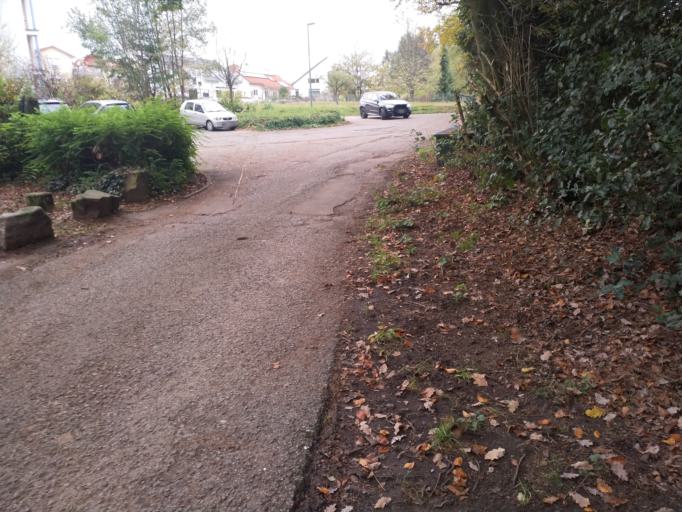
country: DE
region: Baden-Wuerttemberg
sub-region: Karlsruhe Region
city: Engelsbrand
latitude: 48.8549
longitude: 8.6522
